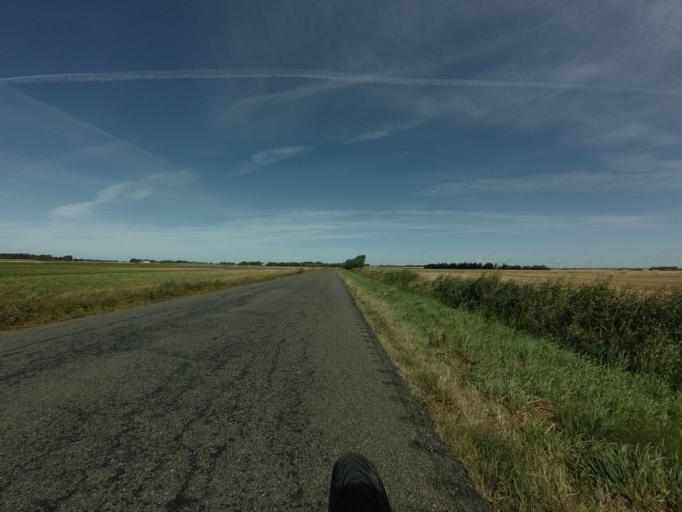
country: DK
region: North Denmark
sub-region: Bronderslev Kommune
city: Bronderslev
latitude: 57.3136
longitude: 9.8126
